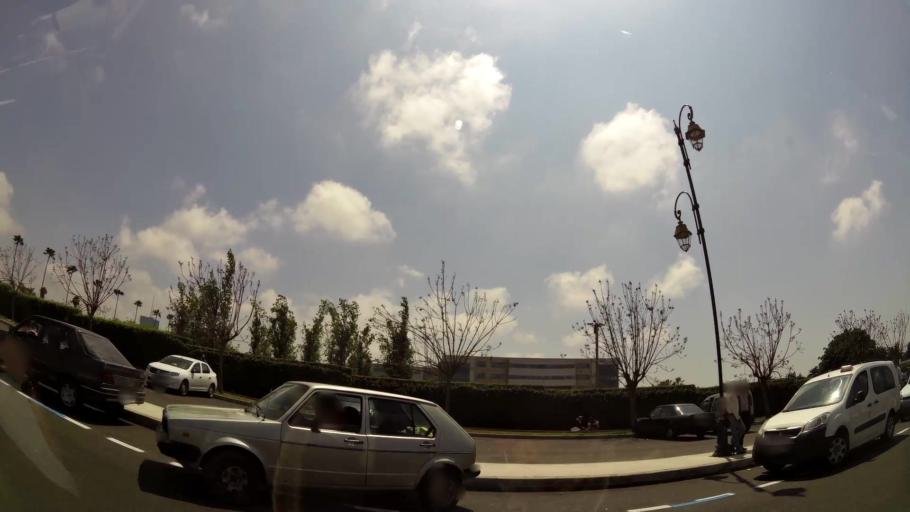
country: MA
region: Rabat-Sale-Zemmour-Zaer
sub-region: Skhirate-Temara
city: Temara
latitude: 33.9669
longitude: -6.8708
